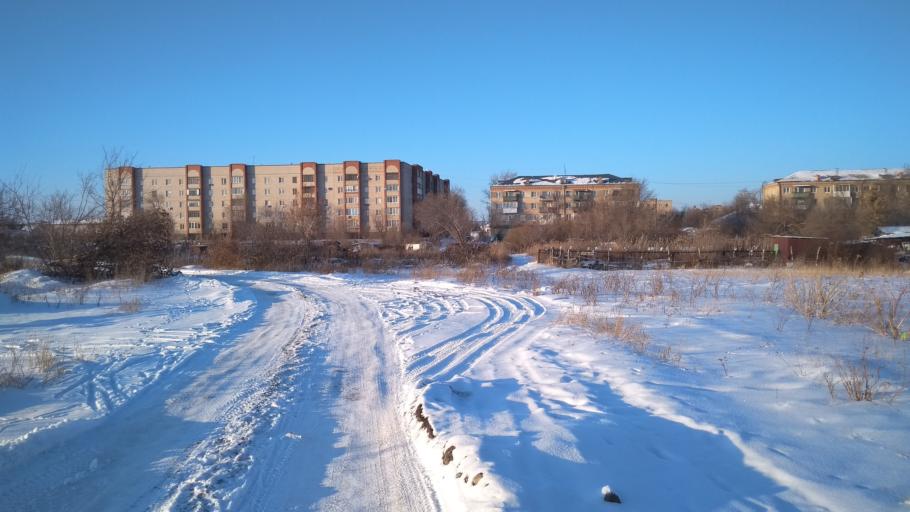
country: RU
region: Chelyabinsk
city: Troitsk
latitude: 54.0829
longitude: 61.5767
